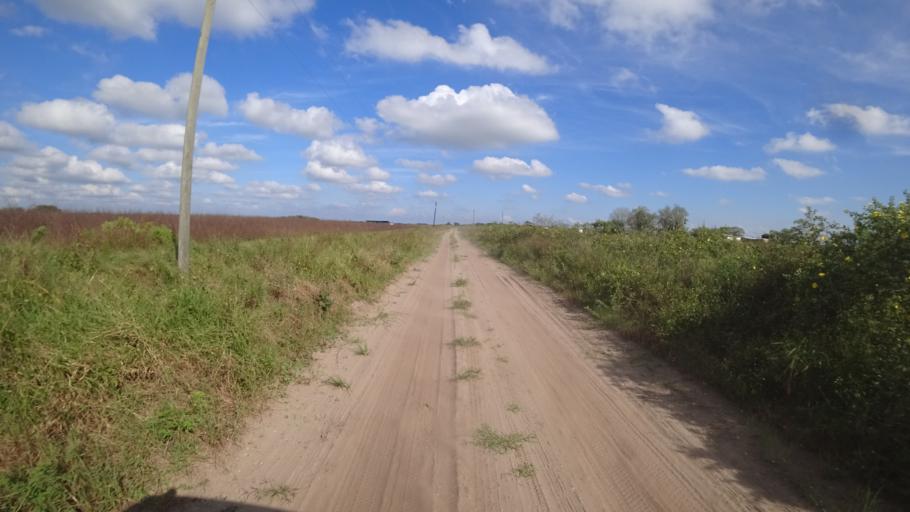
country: US
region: Florida
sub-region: DeSoto County
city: Arcadia
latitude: 27.3463
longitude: -82.1075
